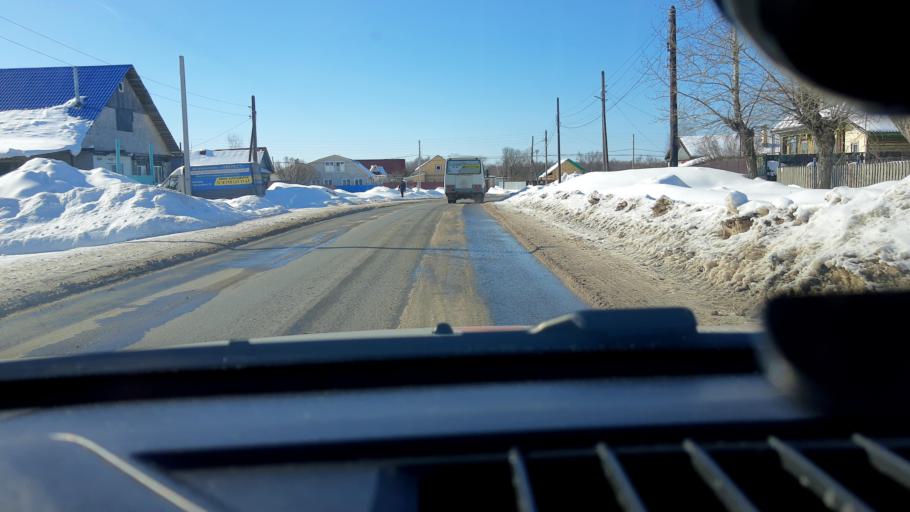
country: RU
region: Nizjnij Novgorod
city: Volodarsk
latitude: 56.2303
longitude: 43.2003
